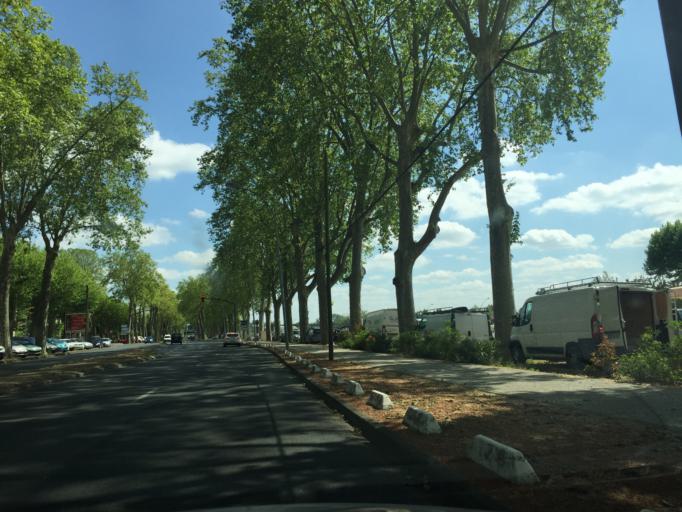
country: FR
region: Aquitaine
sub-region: Departement du Lot-et-Garonne
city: Le Passage
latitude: 44.2014
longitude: 0.6118
